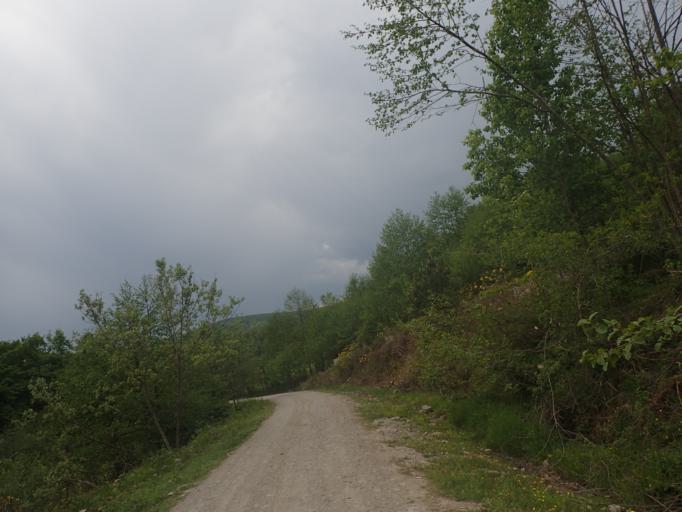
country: TR
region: Ordu
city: Akkus
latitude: 40.8800
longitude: 37.0611
